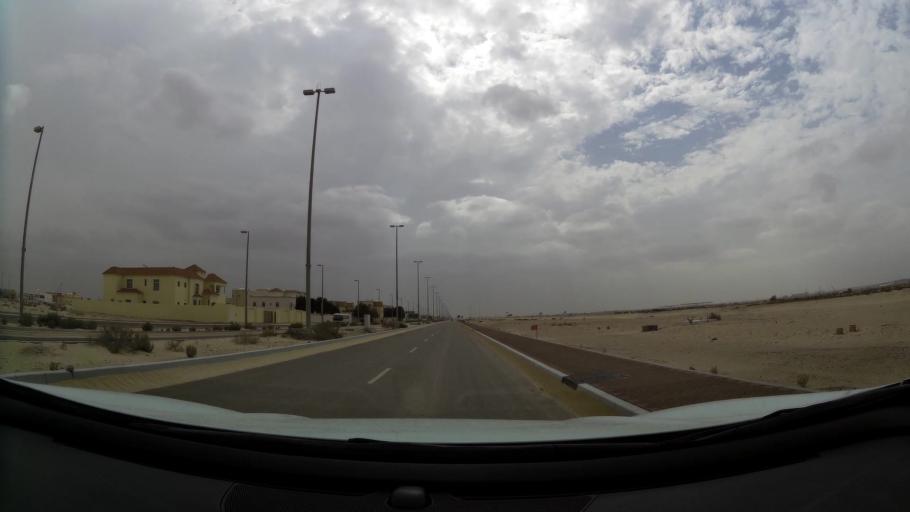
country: AE
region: Abu Dhabi
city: Abu Dhabi
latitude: 24.3998
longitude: 54.6494
